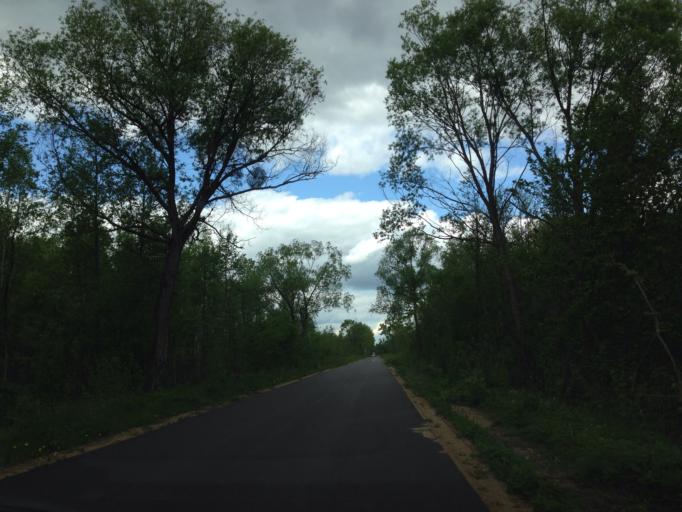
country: PL
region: Podlasie
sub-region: Powiat bialostocki
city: Tykocin
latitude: 53.3040
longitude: 22.6042
